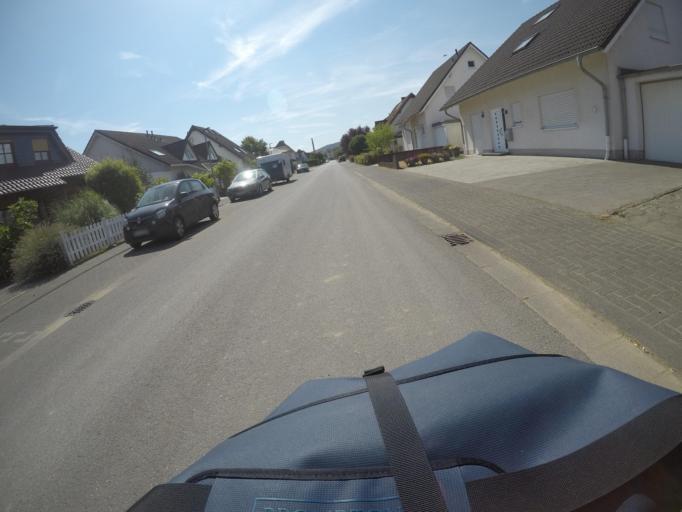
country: DE
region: Rheinland-Pfalz
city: Sinzig
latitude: 50.5513
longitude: 7.2589
